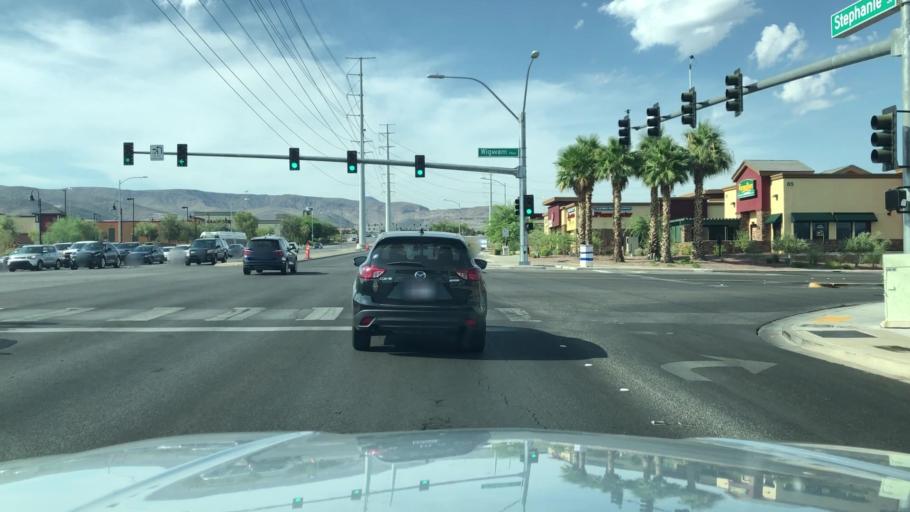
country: US
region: Nevada
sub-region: Clark County
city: Whitney
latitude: 36.0347
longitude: -115.0471
